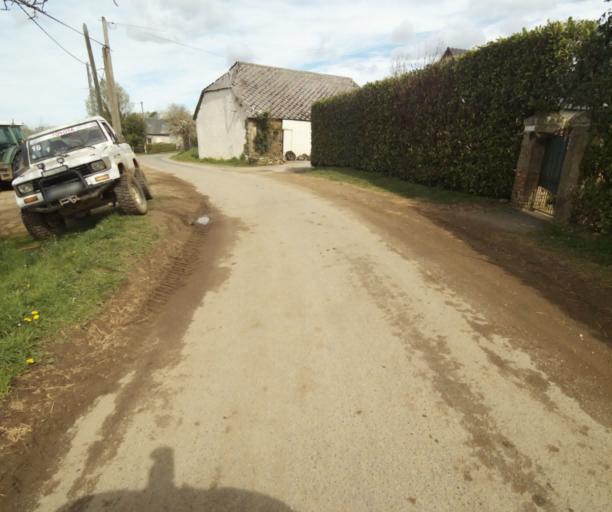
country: FR
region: Limousin
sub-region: Departement de la Correze
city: Laguenne
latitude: 45.2430
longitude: 1.8357
